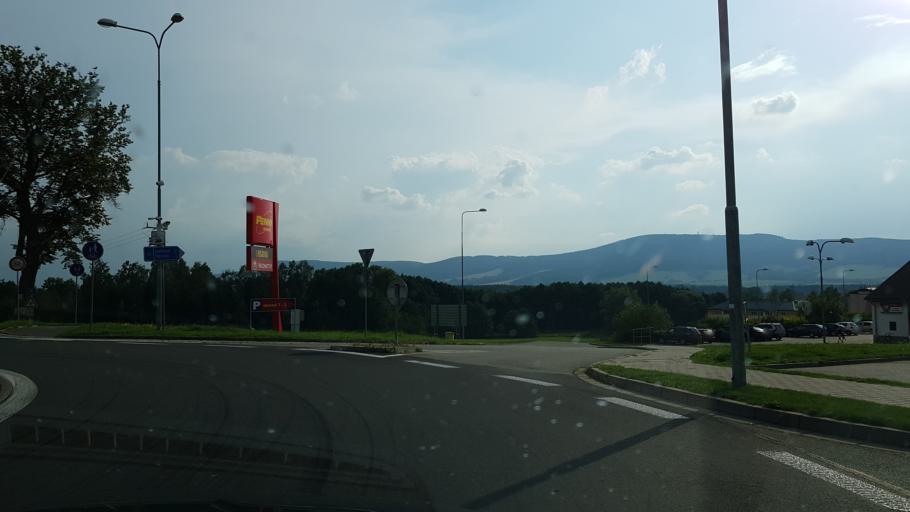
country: CZ
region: Pardubicky
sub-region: Okres Usti nad Orlici
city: Kraliky
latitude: 50.0813
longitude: 16.7614
